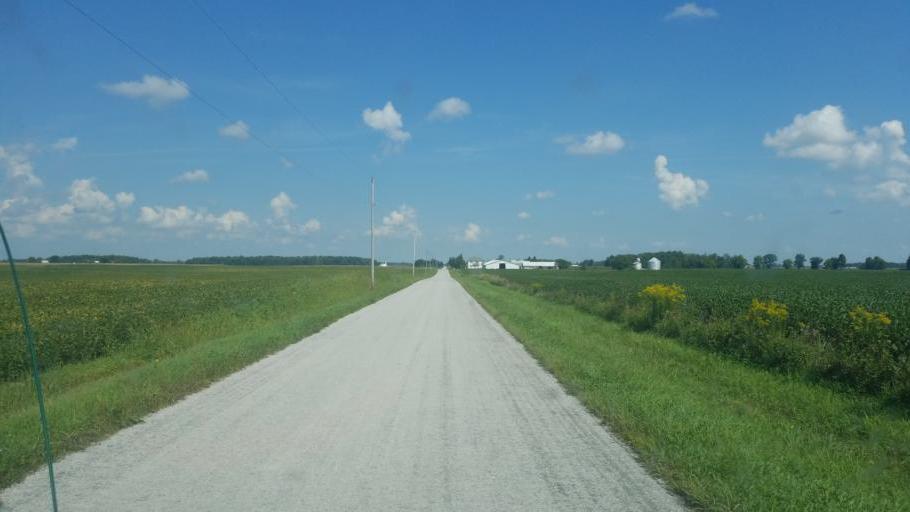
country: US
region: Ohio
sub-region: Hardin County
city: Kenton
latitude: 40.6731
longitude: -83.4957
